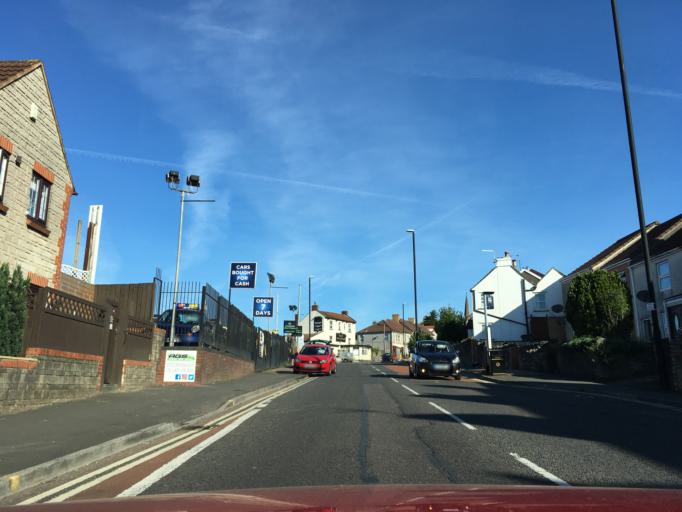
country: GB
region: England
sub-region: South Gloucestershire
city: Kingswood
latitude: 51.4517
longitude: -2.5223
